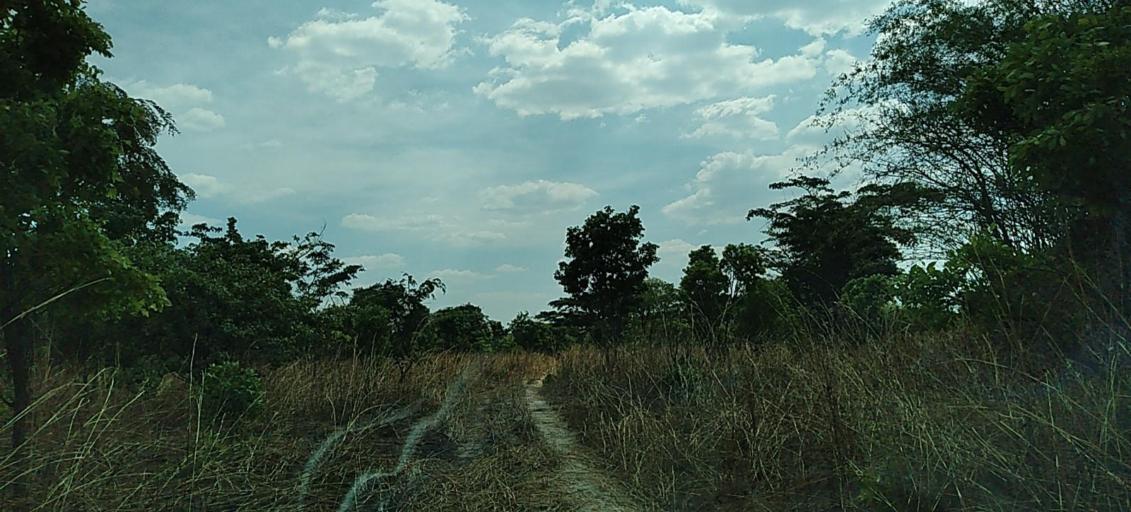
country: ZM
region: Copperbelt
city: Chililabombwe
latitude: -12.3307
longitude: 27.7664
